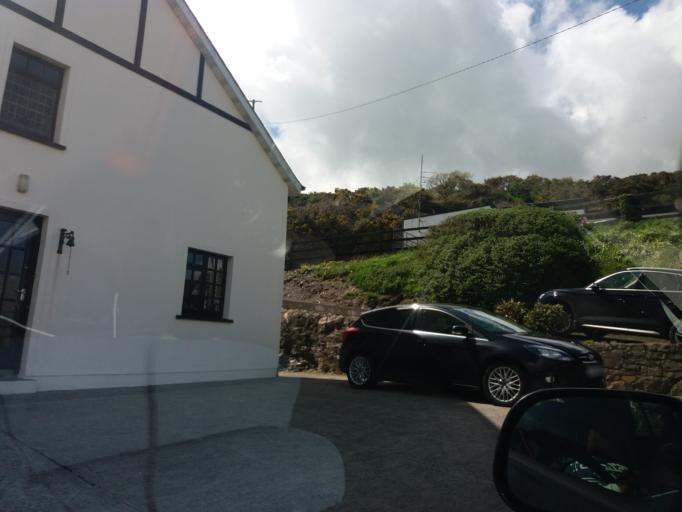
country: IE
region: Munster
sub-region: Waterford
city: Dunmore East
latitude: 52.2432
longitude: -6.9558
